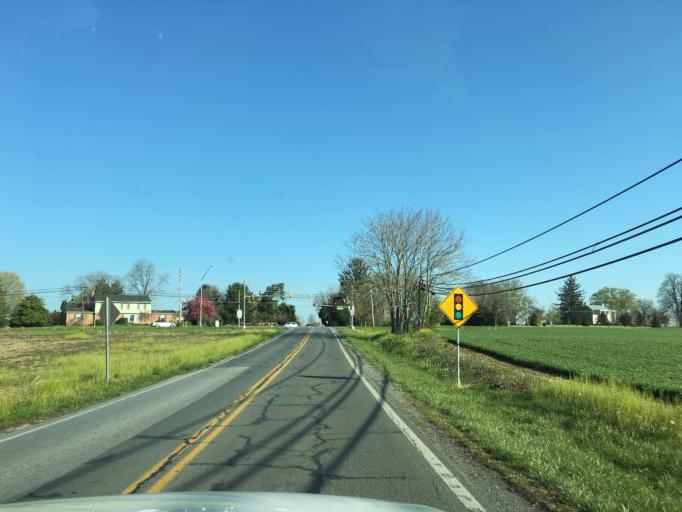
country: US
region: Maryland
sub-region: Frederick County
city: Walkersville
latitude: 39.4916
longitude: -77.3319
